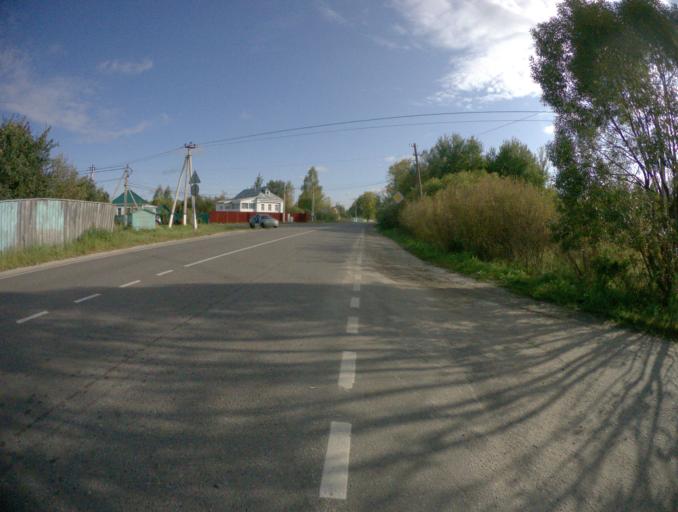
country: RU
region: Moskovskaya
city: Roshal'
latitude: 55.6571
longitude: 39.8286
